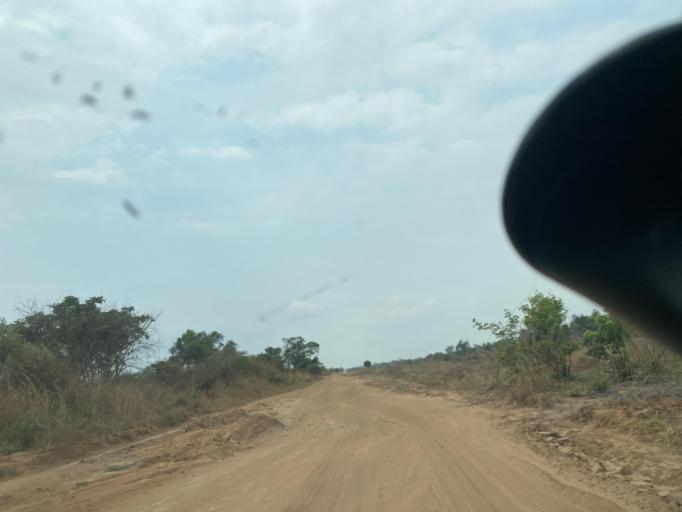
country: ZM
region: Lusaka
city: Lusaka
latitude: -15.2000
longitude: 28.3416
